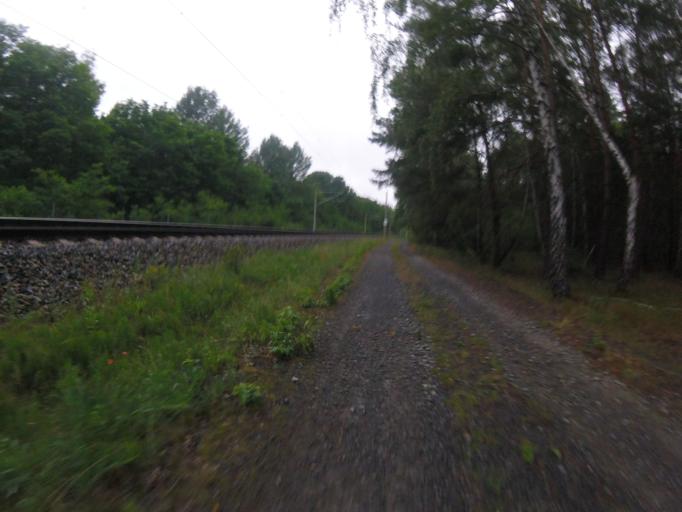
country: DE
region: Brandenburg
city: Bestensee
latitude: 52.2135
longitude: 13.6179
